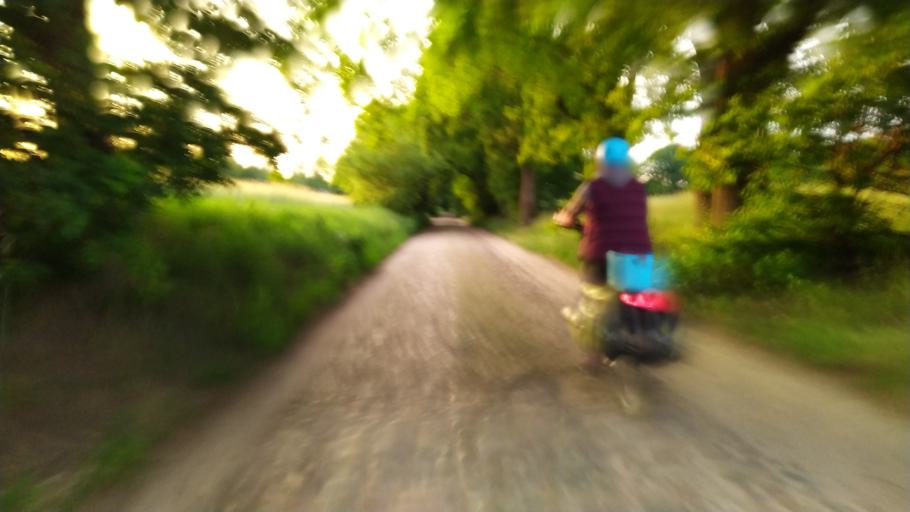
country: DE
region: Lower Saxony
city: Neu Wulmstorf
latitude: 53.4765
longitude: 9.8287
